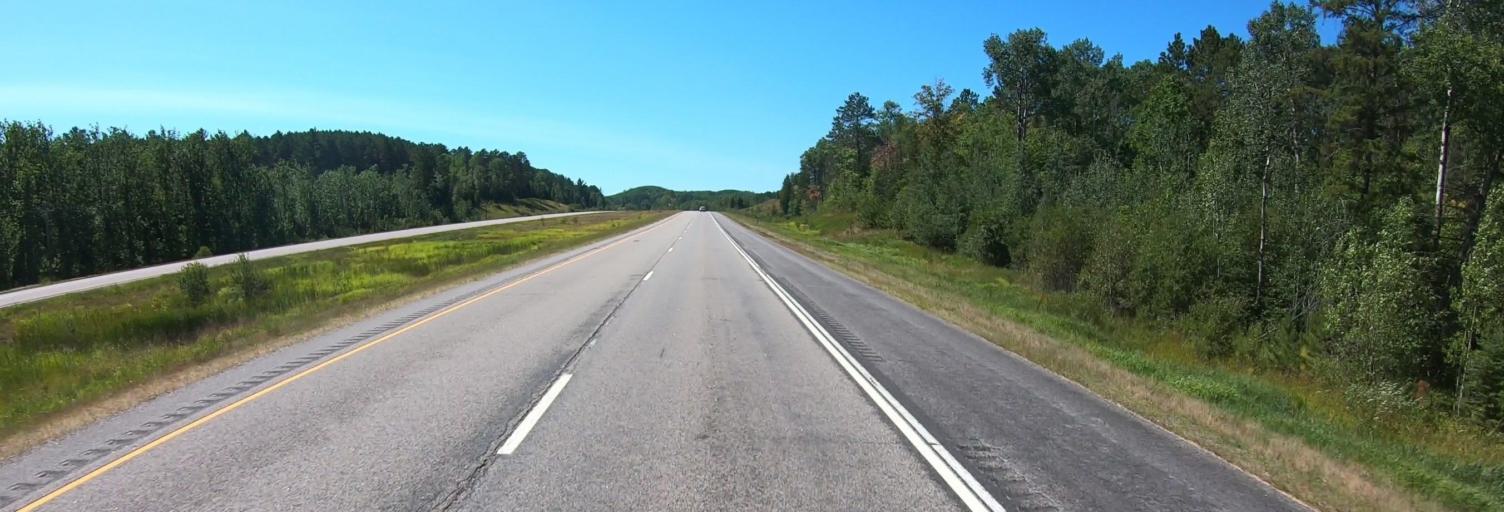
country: US
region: Minnesota
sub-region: Saint Louis County
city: Mountain Iron
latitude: 47.6926
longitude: -92.6491
